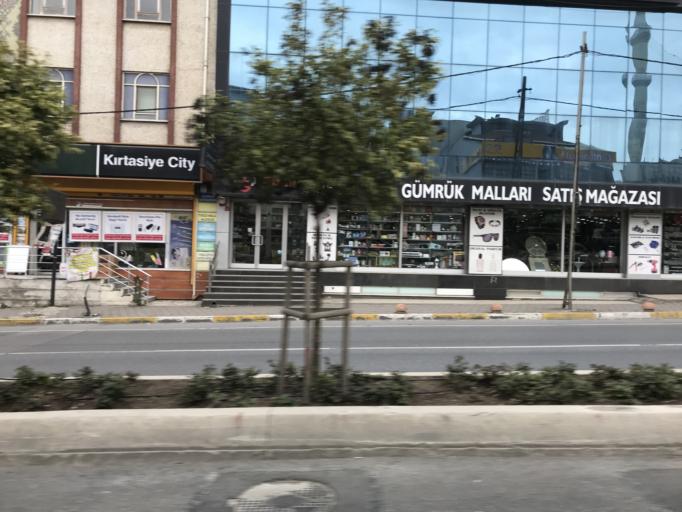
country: TR
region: Istanbul
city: Umraniye
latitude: 41.0080
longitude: 29.1625
